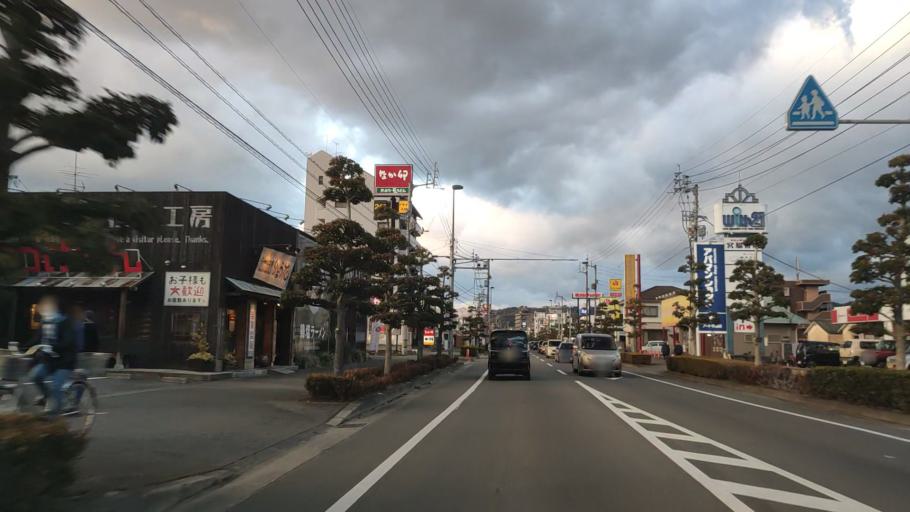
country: JP
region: Ehime
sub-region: Shikoku-chuo Shi
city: Matsuyama
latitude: 33.8338
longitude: 132.7872
